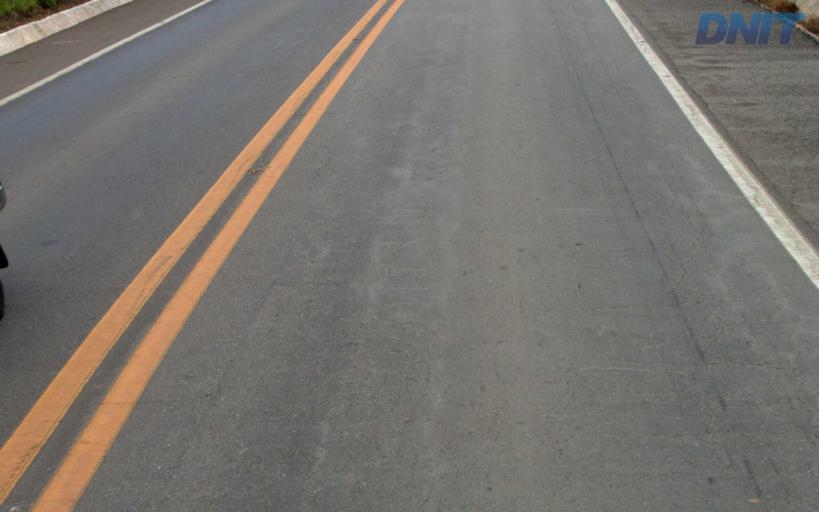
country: BR
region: Minas Gerais
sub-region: Governador Valadares
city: Governador Valadares
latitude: -19.0111
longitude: -42.1382
